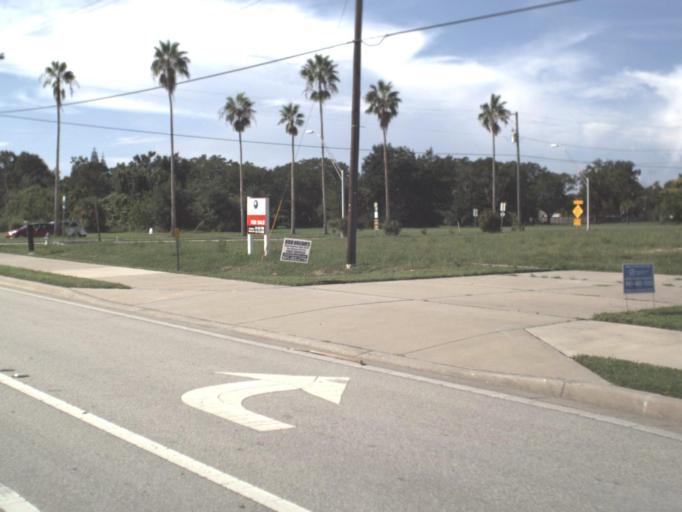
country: US
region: Florida
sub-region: Sarasota County
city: Nokomis
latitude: 27.1254
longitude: -82.4537
